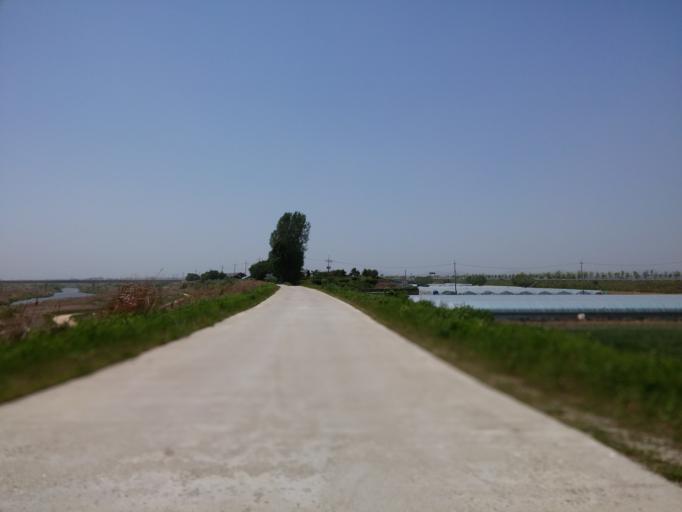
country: KR
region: Chungcheongnam-do
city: Nonsan
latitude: 36.2156
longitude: 127.1070
